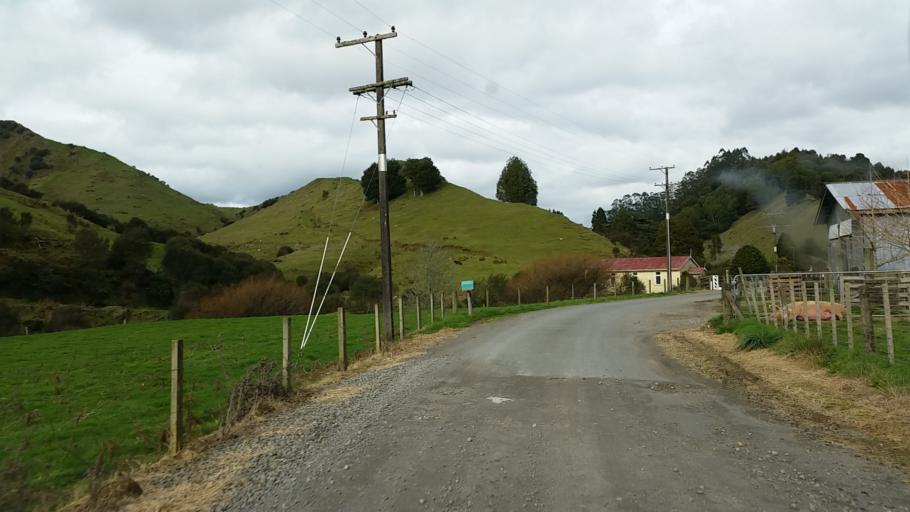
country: NZ
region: Taranaki
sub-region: New Plymouth District
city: Waitara
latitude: -39.1584
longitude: 174.5624
